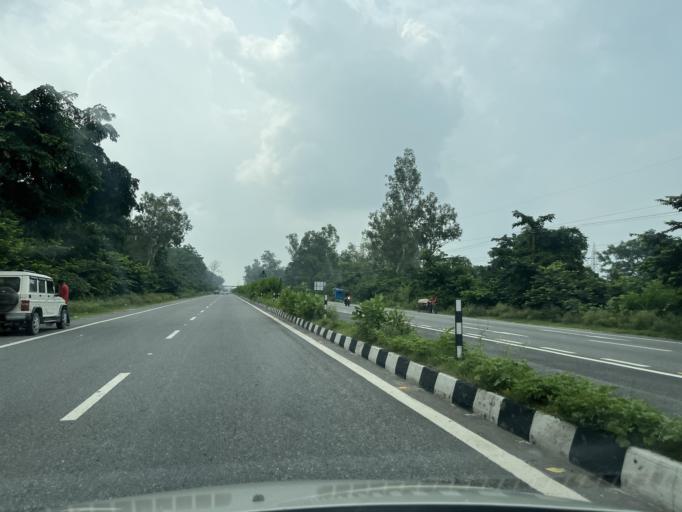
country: IN
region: Uttarakhand
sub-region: Dehradun
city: Doiwala
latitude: 30.1115
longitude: 78.1699
